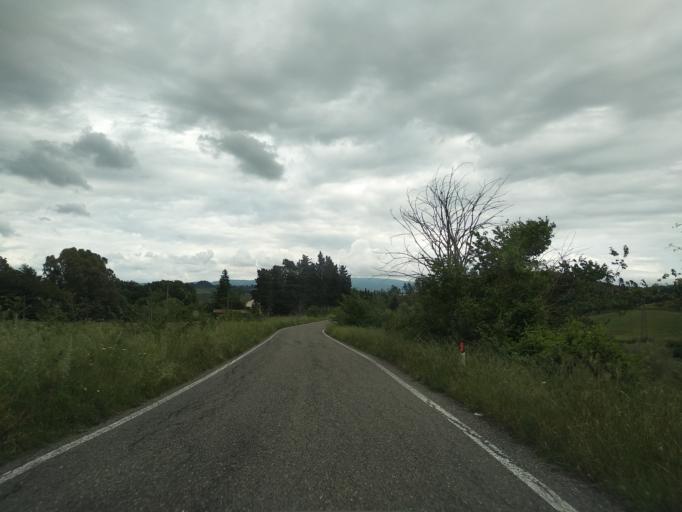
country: IT
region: Tuscany
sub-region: Provincia di Livorno
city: Collesalvetti
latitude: 43.5410
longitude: 10.4520
